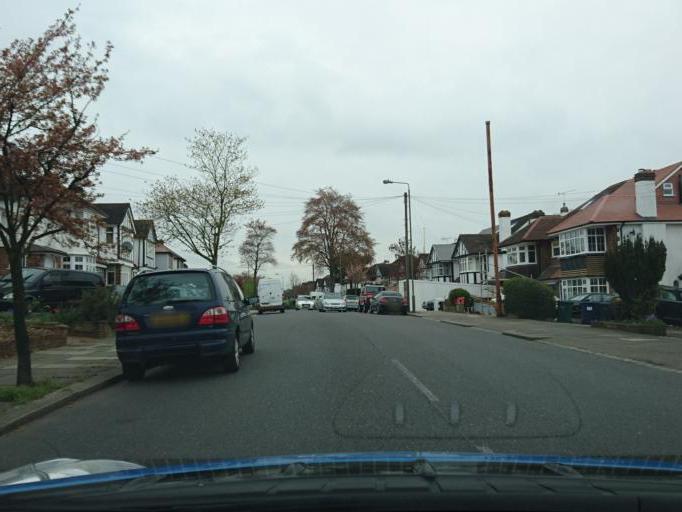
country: GB
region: England
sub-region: Greater London
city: Barnet
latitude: 51.6272
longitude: -0.1841
